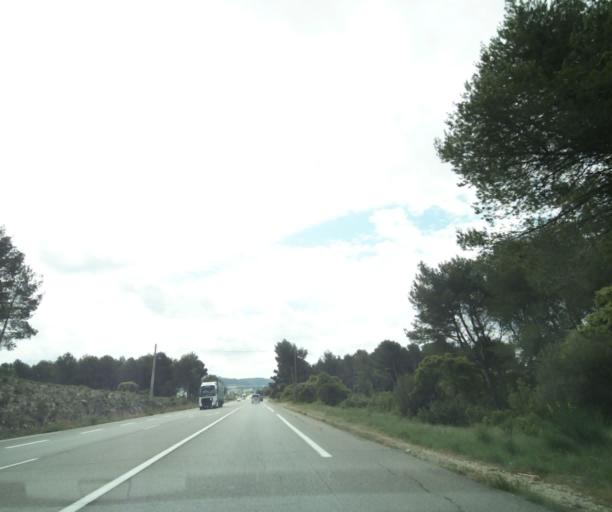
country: FR
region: Provence-Alpes-Cote d'Azur
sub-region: Departement des Bouches-du-Rhone
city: Rognac
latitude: 43.5050
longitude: 5.2089
